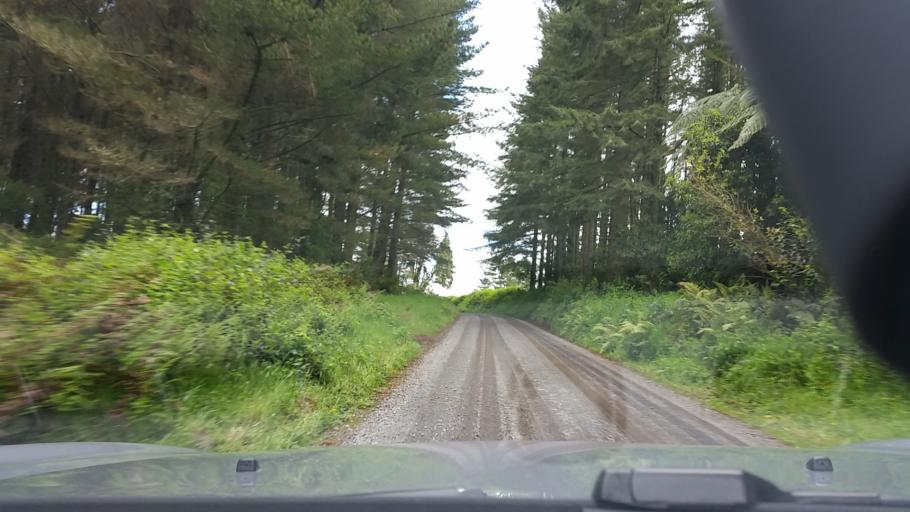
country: NZ
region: Bay of Plenty
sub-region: Whakatane District
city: Murupara
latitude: -38.3471
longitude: 176.5384
